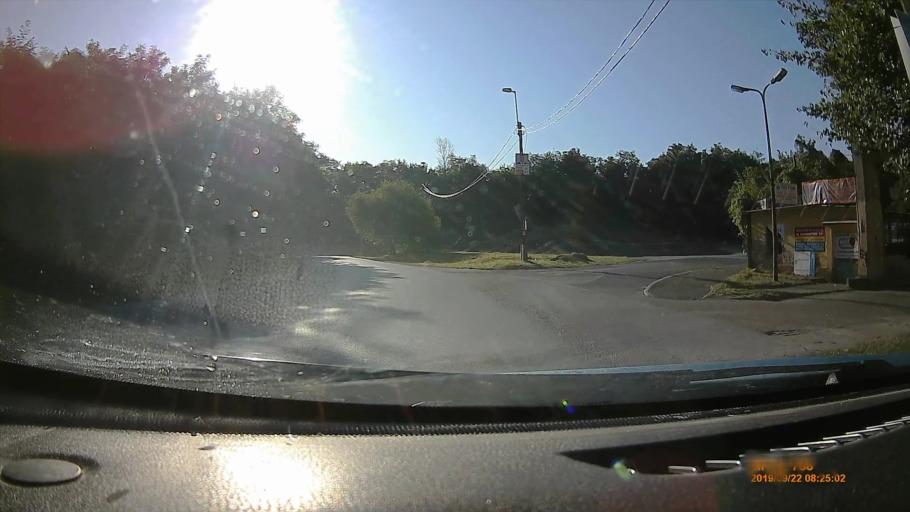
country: HU
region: Borsod-Abauj-Zemplen
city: Miskolc
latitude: 48.0877
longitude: 20.7151
